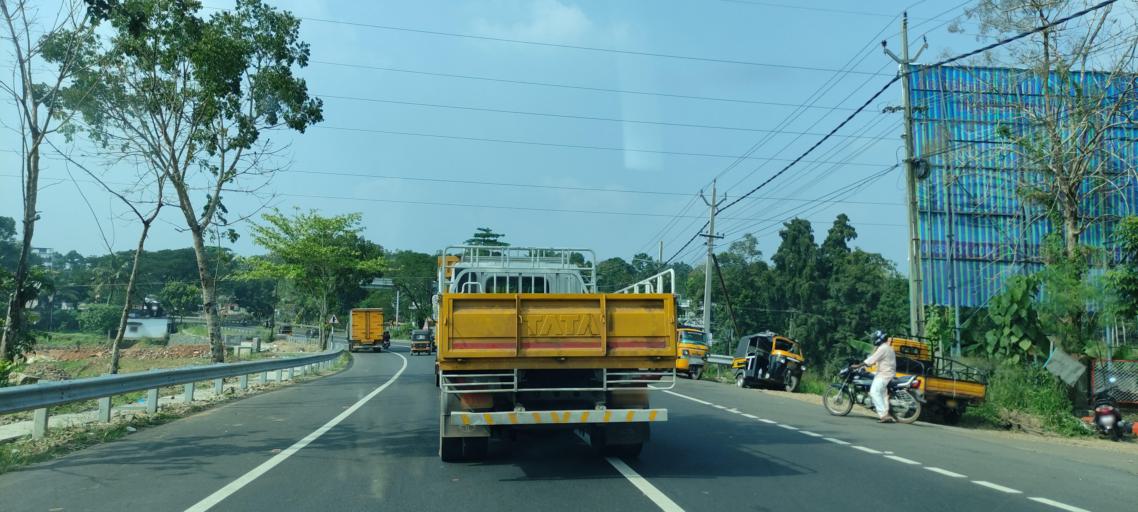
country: IN
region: Kerala
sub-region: Alappuzha
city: Chengannur
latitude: 9.2484
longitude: 76.6681
